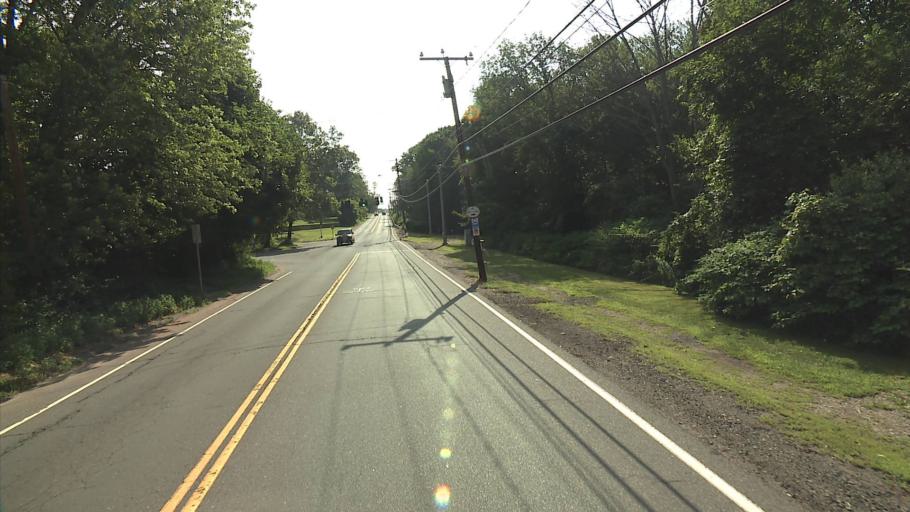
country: US
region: Connecticut
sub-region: New Haven County
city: Wolcott
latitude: 41.5544
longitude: -72.9650
